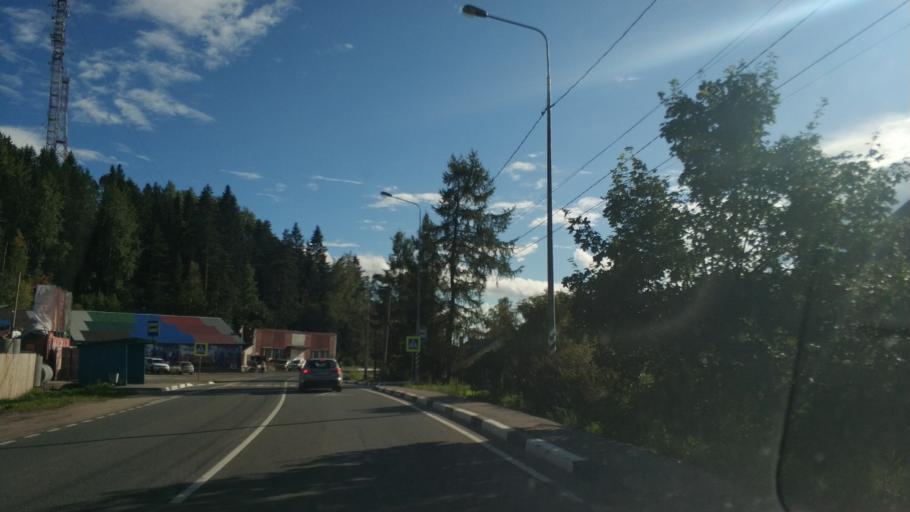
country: RU
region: Republic of Karelia
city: Lakhdenpokh'ya
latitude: 61.5262
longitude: 30.2017
